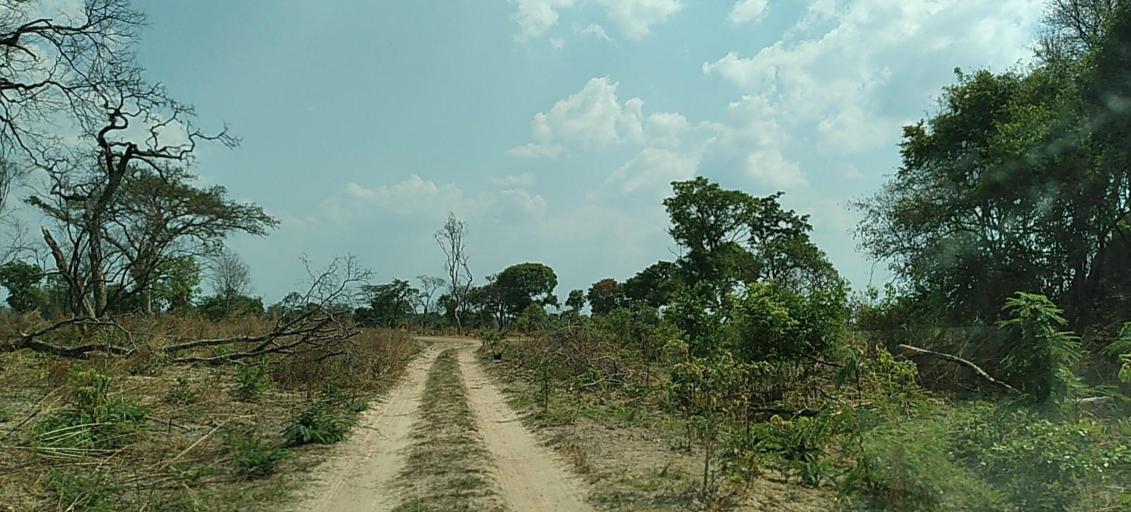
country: ZM
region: Copperbelt
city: Mpongwe
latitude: -13.8709
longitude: 27.9239
